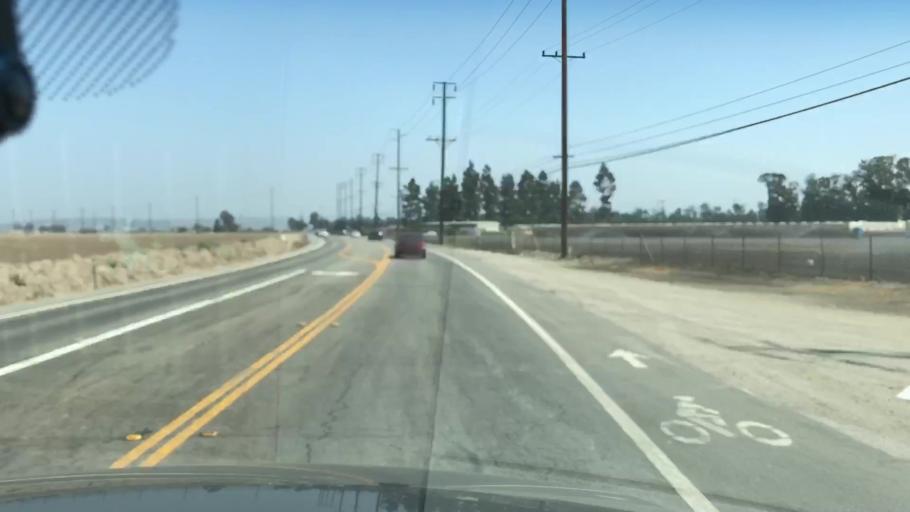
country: US
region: California
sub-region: Ventura County
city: Oxnard
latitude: 34.1751
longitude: -119.1248
